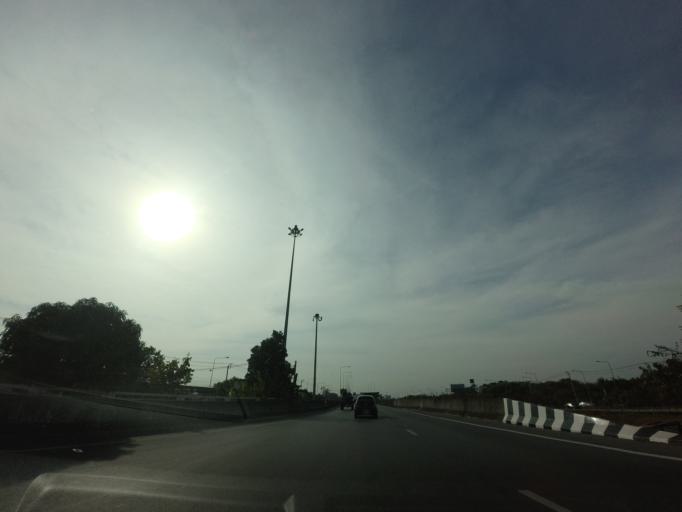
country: TH
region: Bangkok
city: Sai Mai
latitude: 13.8969
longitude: 100.6835
